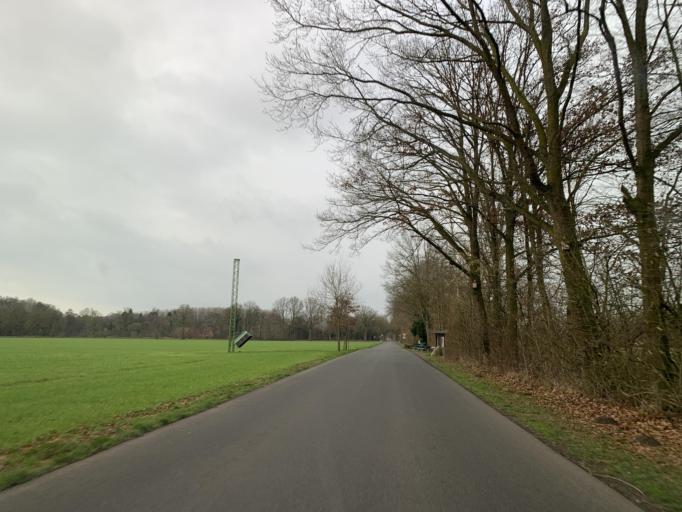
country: DE
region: North Rhine-Westphalia
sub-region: Regierungsbezirk Munster
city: Senden
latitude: 51.8895
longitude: 7.4764
